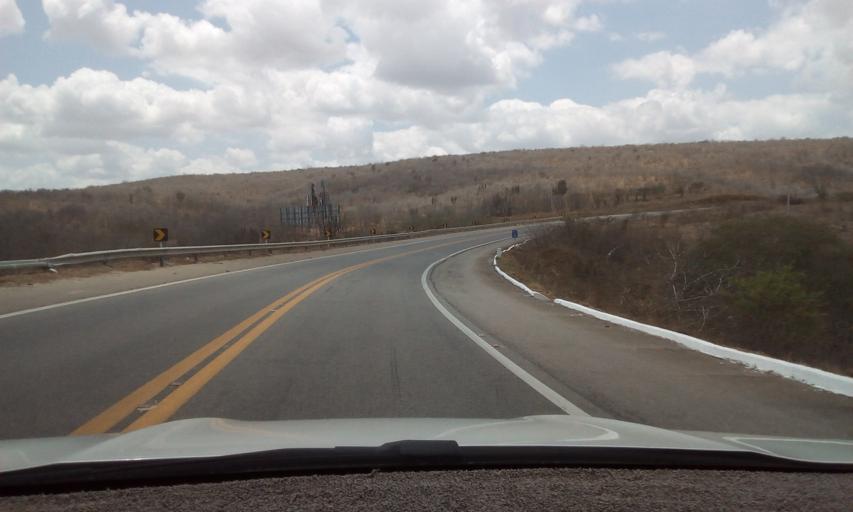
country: BR
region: Paraiba
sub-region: Boqueirao
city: Boqueirao
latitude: -7.6801
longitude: -36.0609
